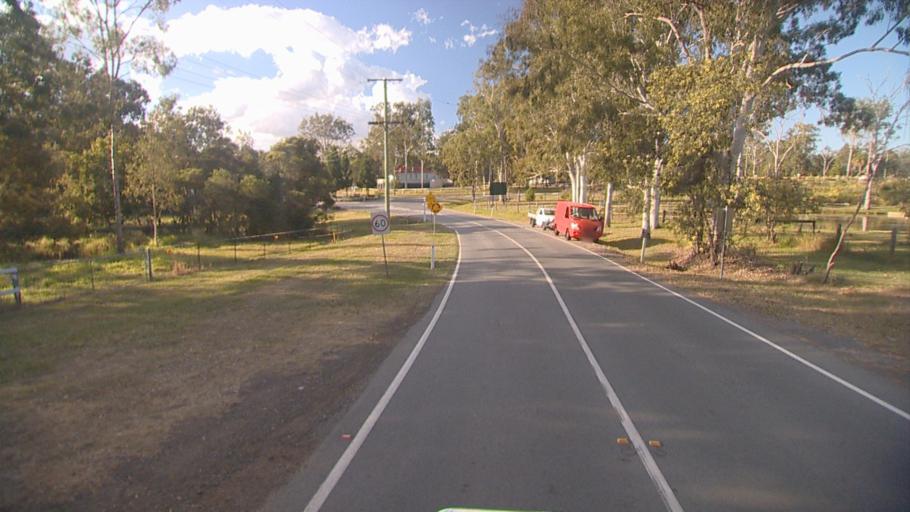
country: AU
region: Queensland
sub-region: Ipswich
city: Springfield Lakes
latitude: -27.7340
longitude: 152.9464
